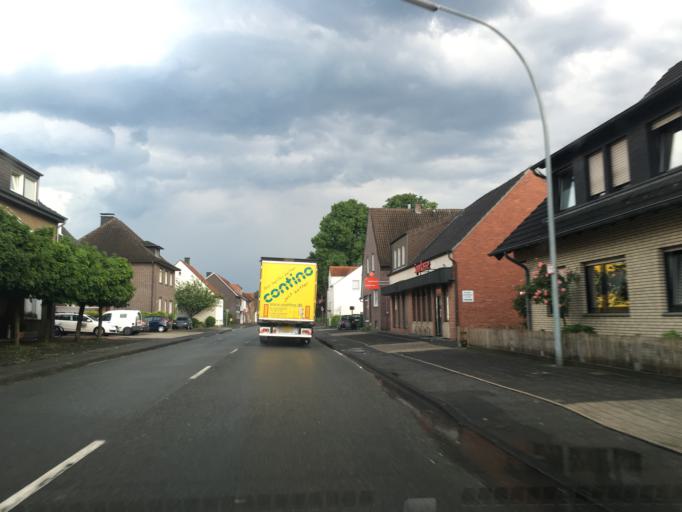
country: DE
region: North Rhine-Westphalia
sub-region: Regierungsbezirk Munster
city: Laer
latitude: 52.1125
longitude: 7.3999
